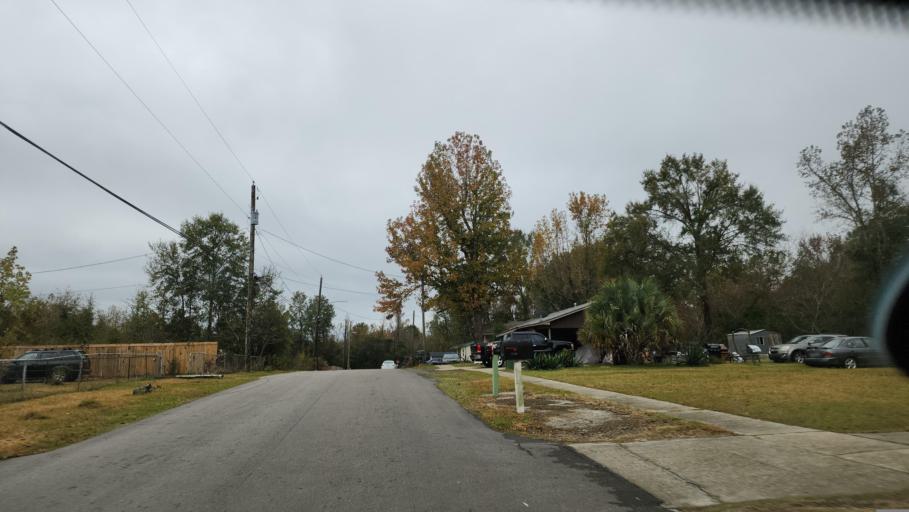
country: US
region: Mississippi
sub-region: Forrest County
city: Hattiesburg
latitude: 31.3008
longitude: -89.3036
